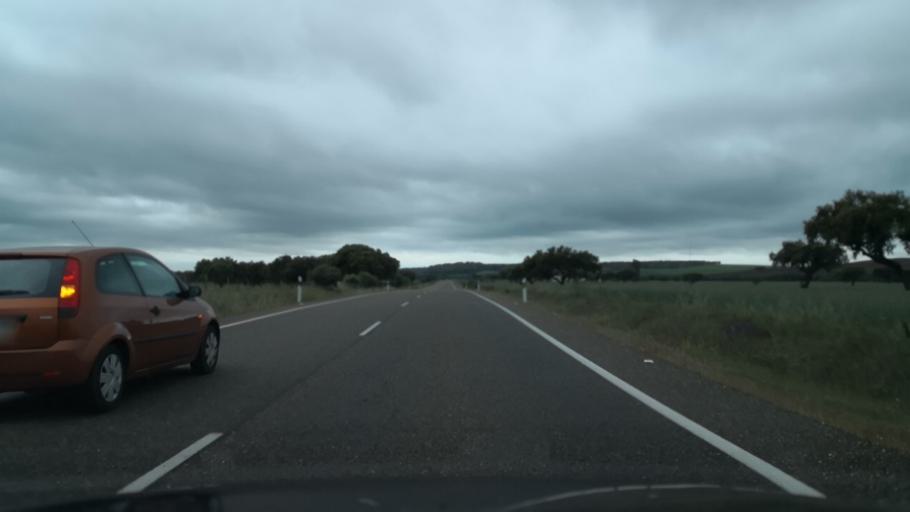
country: ES
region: Extremadura
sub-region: Provincia de Badajoz
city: La Roca de la Sierra
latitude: 39.0647
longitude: -6.7633
